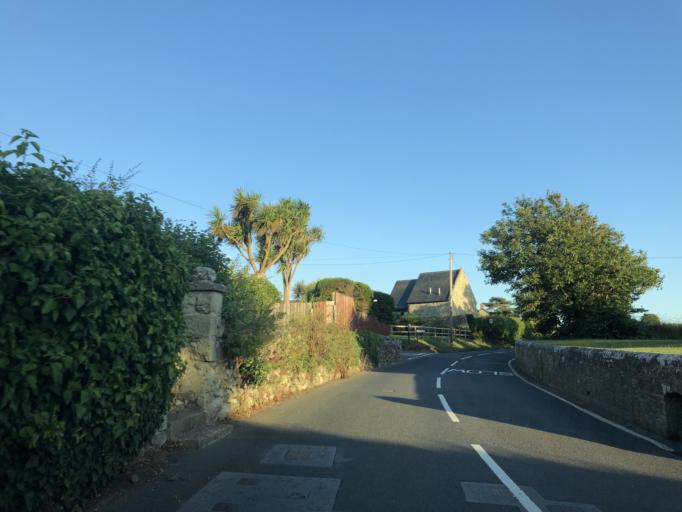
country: GB
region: England
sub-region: Isle of Wight
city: Chale
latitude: 50.6099
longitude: -1.3196
